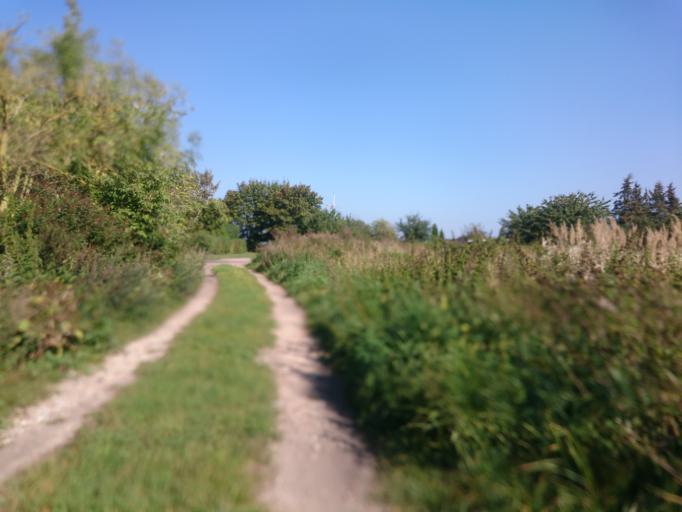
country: DE
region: Mecklenburg-Vorpommern
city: Barth
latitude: 54.3727
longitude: 12.7119
